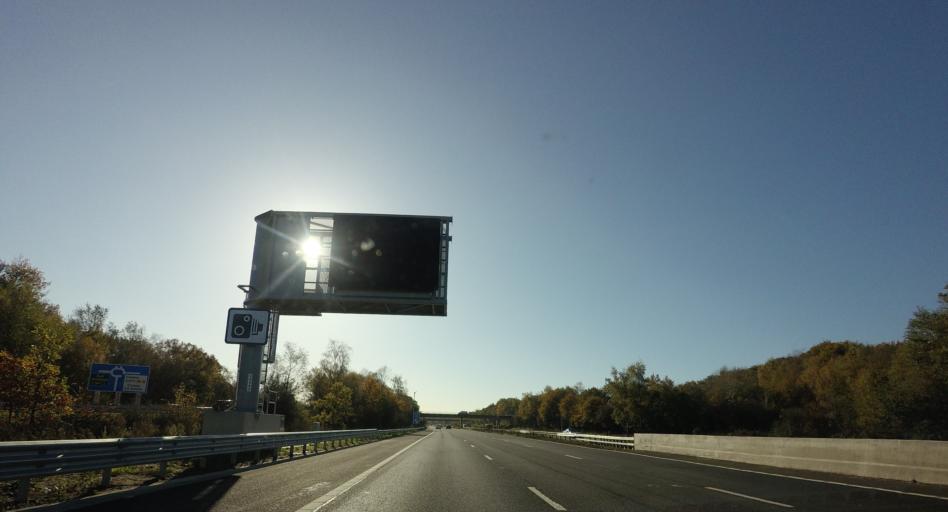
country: GB
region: England
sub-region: West Sussex
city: Copthorne
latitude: 51.1348
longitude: -0.1406
